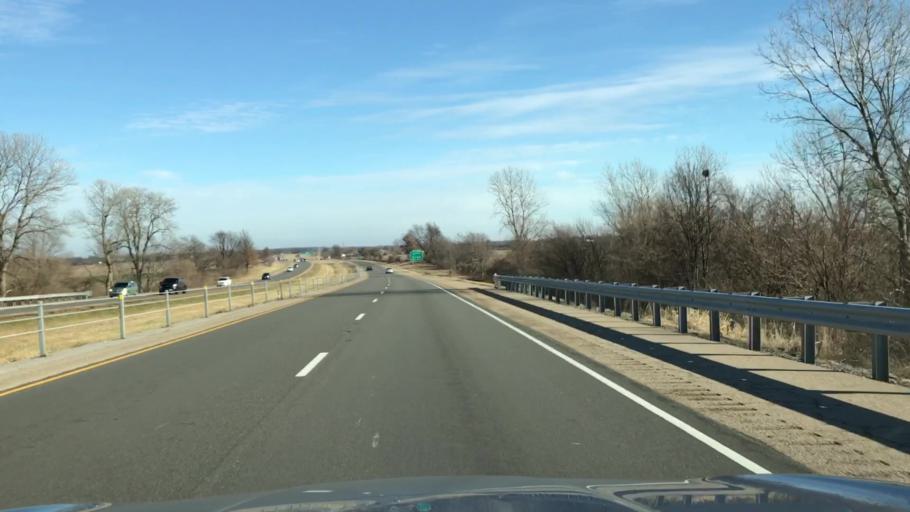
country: US
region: Illinois
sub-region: Madison County
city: Maryville
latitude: 38.7517
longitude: -89.9254
